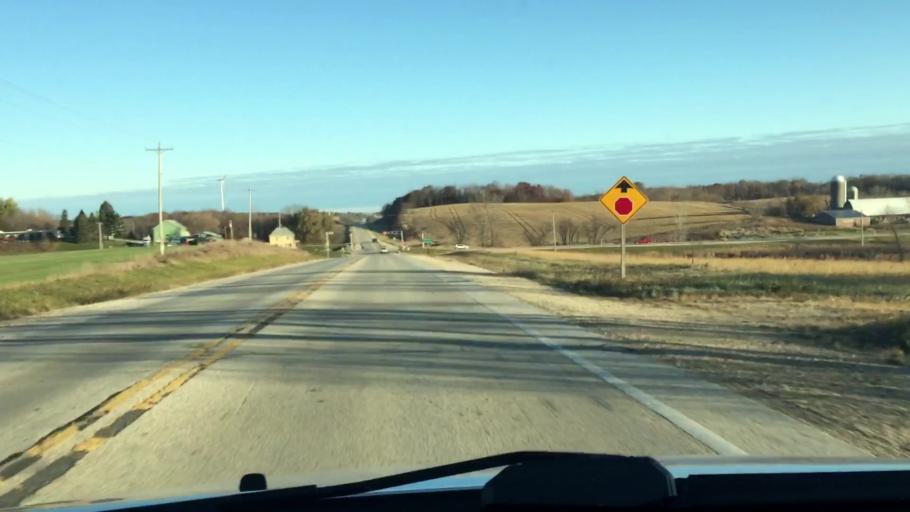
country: US
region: Wisconsin
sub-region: Dodge County
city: Theresa
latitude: 43.4283
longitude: -88.4502
